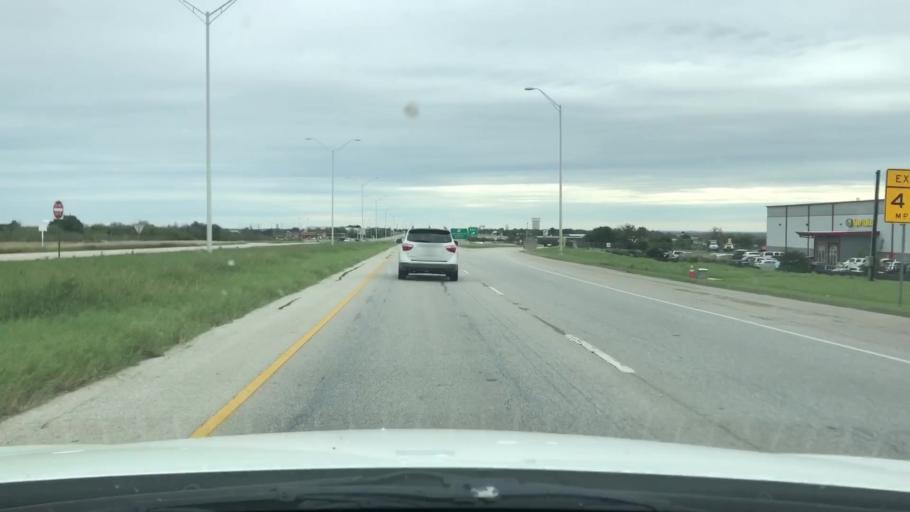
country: US
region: Texas
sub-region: Bexar County
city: Universal City
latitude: 29.5388
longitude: -98.3061
